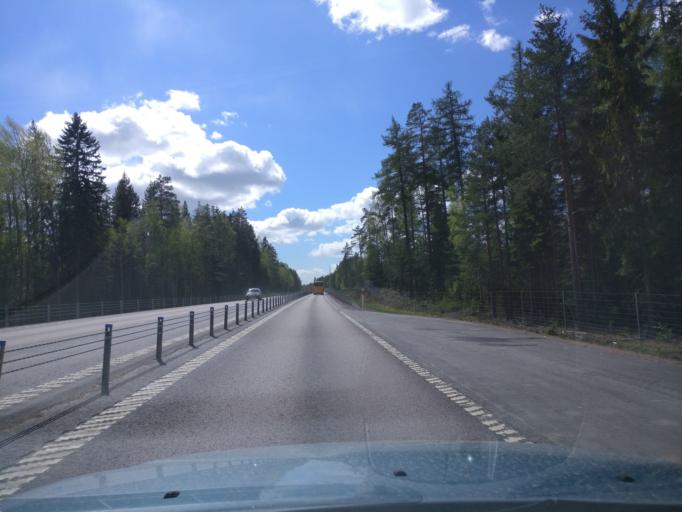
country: SE
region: Vaermland
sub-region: Karlstads Kommun
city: Karlstad
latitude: 59.4338
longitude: 13.5403
